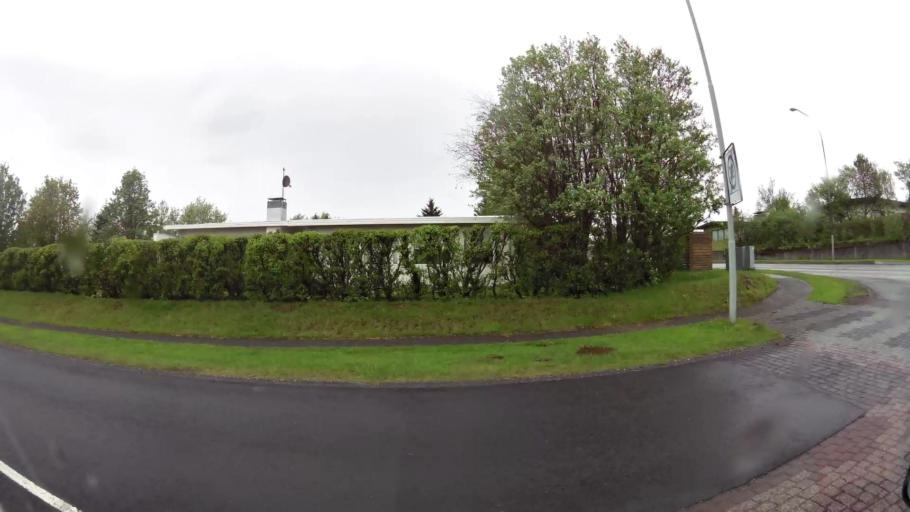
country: IS
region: Capital Region
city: Gardabaer
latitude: 64.0869
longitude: -21.9089
